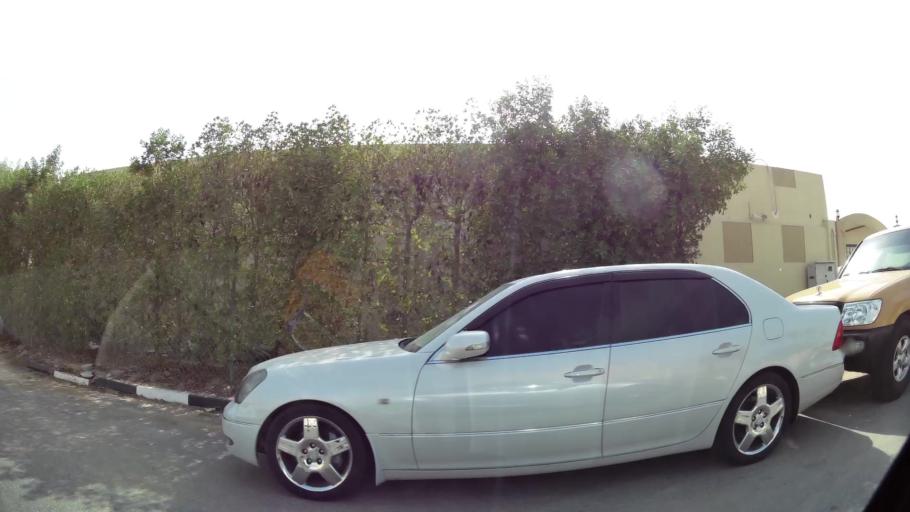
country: AE
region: Ash Shariqah
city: Sharjah
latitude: 25.2589
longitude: 55.4354
